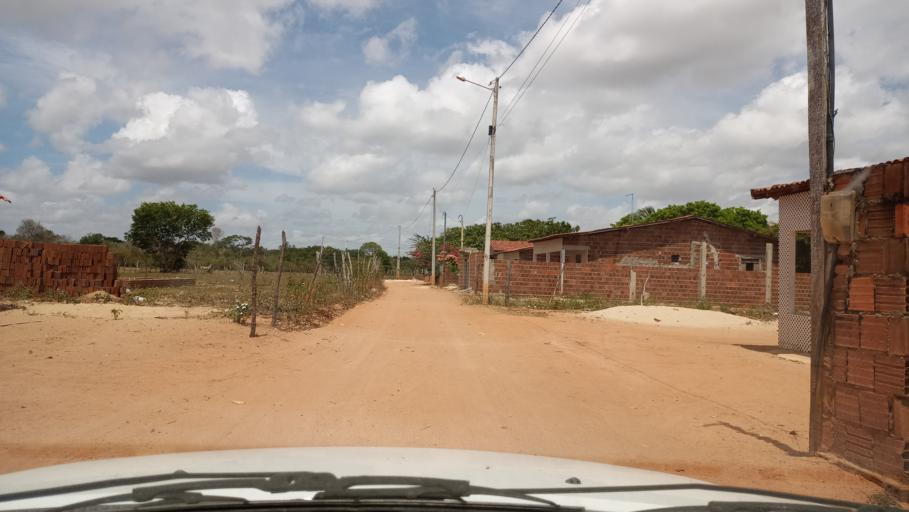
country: BR
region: Rio Grande do Norte
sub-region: Goianinha
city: Goianinha
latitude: -6.2839
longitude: -35.2841
